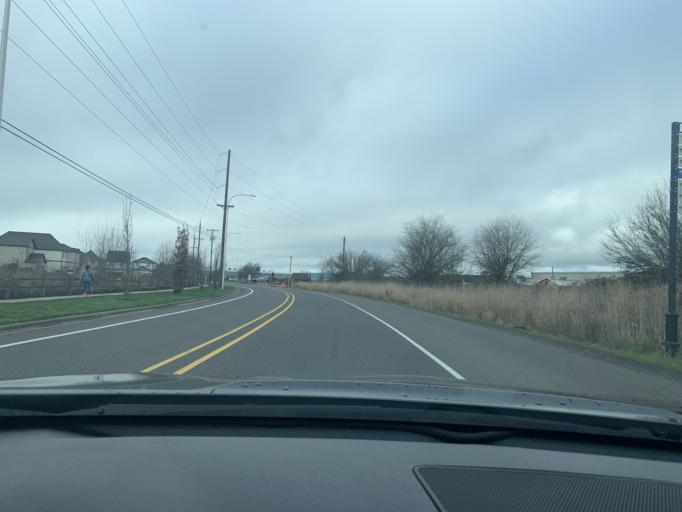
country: US
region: Oregon
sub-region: Washington County
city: North Plains
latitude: 45.5961
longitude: -122.9713
